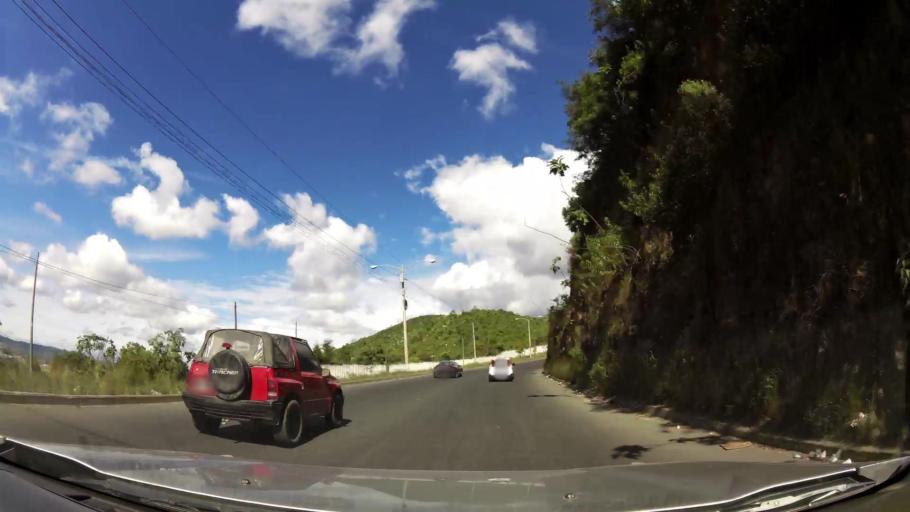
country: GT
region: Guatemala
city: Guatemala City
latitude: 14.6608
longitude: -90.5547
